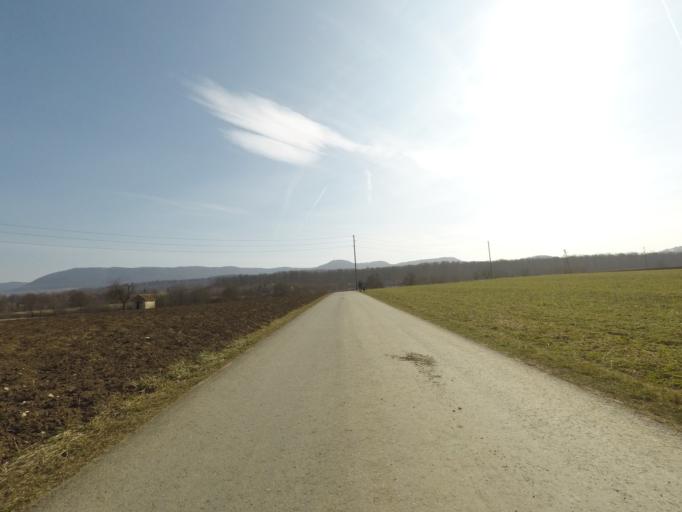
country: DE
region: Baden-Wuerttemberg
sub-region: Tuebingen Region
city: Metzingen
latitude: 48.5319
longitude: 9.2601
